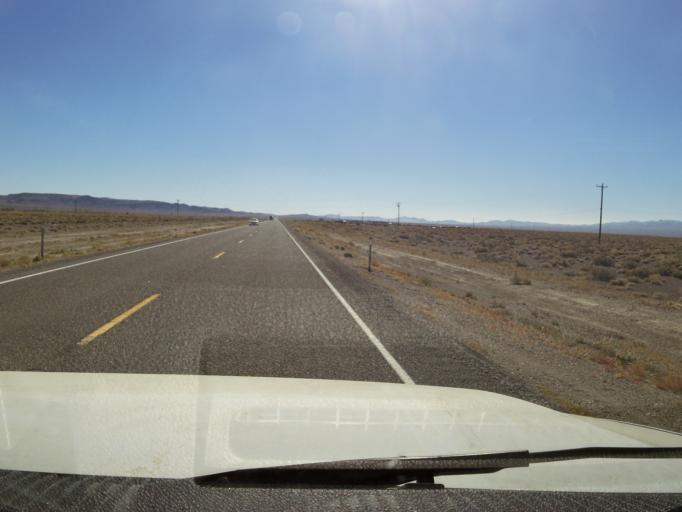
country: US
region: Nevada
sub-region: Esmeralda County
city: Goldfield
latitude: 37.2943
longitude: -117.0488
